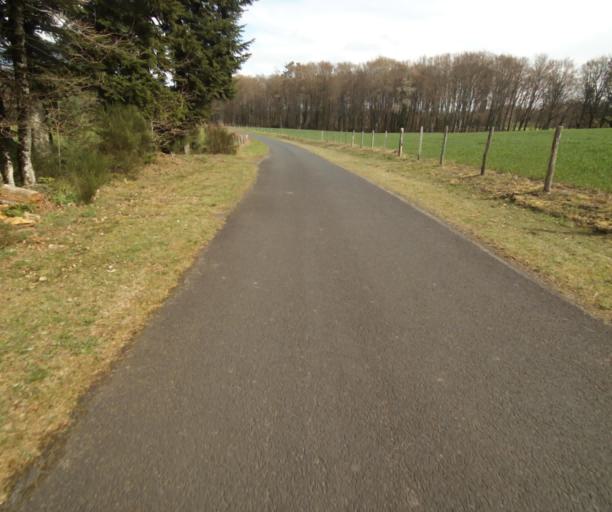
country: FR
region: Limousin
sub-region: Departement de la Correze
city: Correze
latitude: 45.3555
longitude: 1.8981
